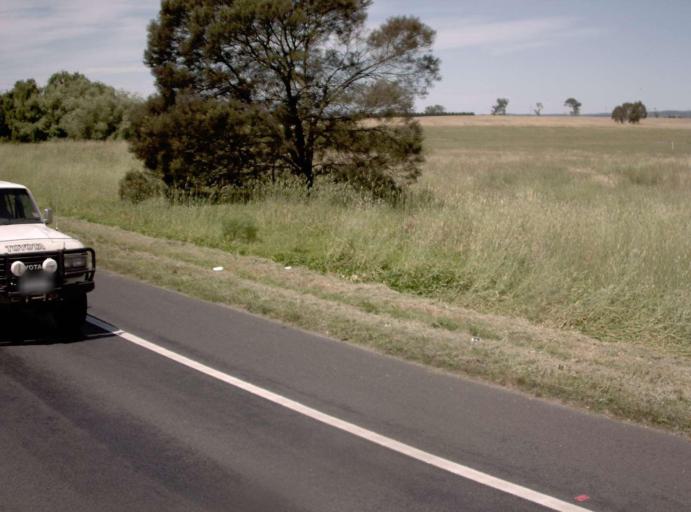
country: AU
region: Victoria
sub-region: Latrobe
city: Traralgon
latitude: -38.1582
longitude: 146.7093
